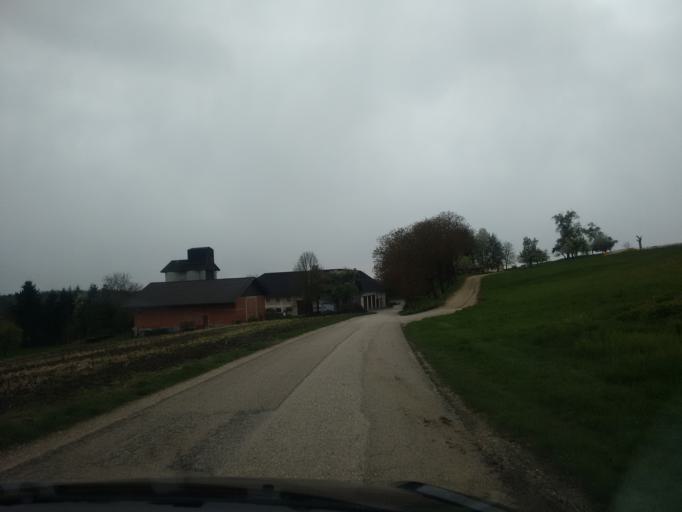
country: AT
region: Upper Austria
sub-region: Wels-Land
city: Buchkirchen
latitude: 48.2083
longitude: 14.0568
